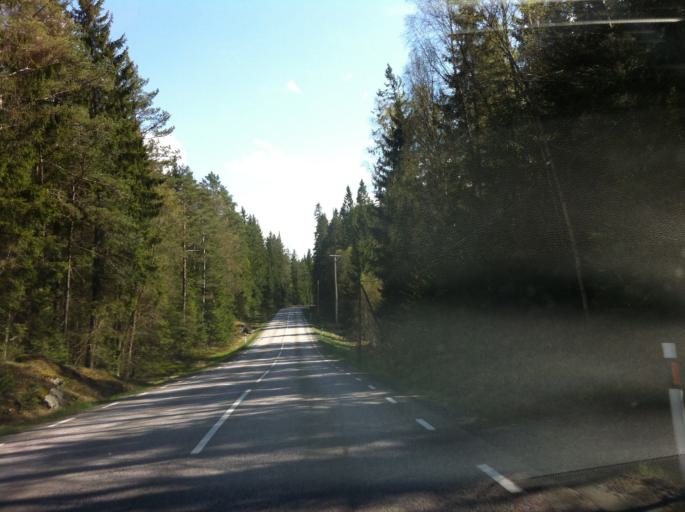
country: SE
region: Vaestra Goetaland
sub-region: Alingsas Kommun
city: Alingsas
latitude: 57.8580
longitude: 12.6157
